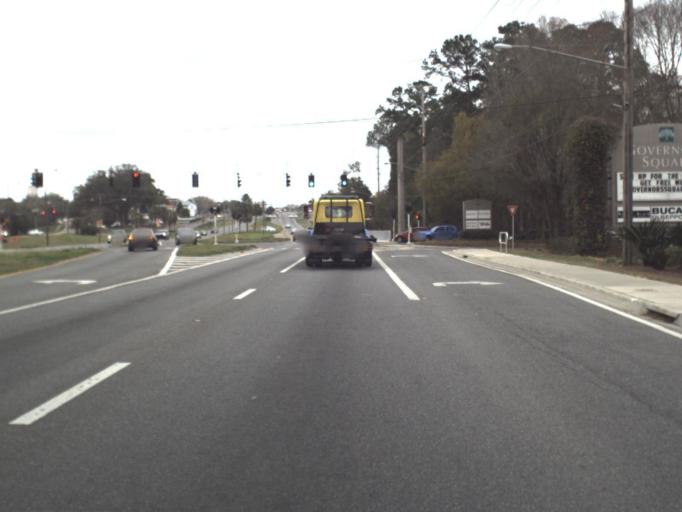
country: US
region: Florida
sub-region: Leon County
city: Tallahassee
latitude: 30.4344
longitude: -84.2548
